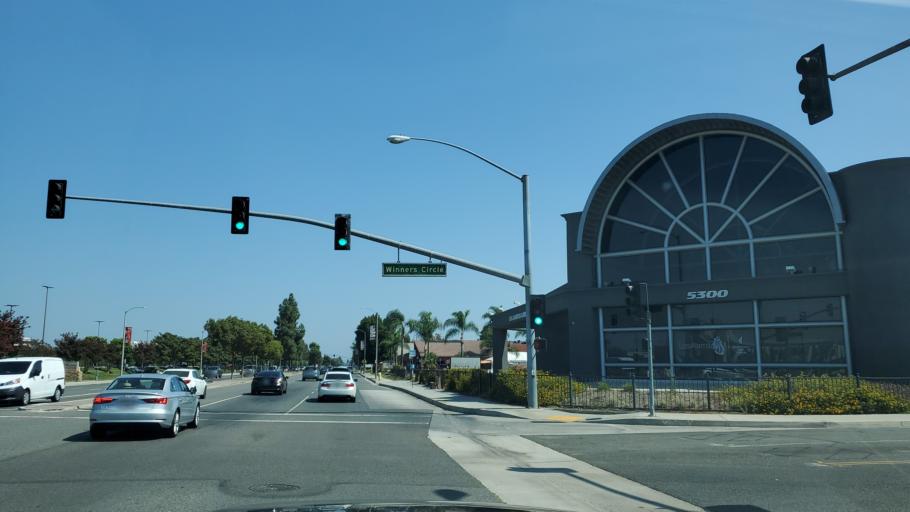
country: US
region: California
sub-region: Orange County
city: Cypress
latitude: 33.8029
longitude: -118.0410
